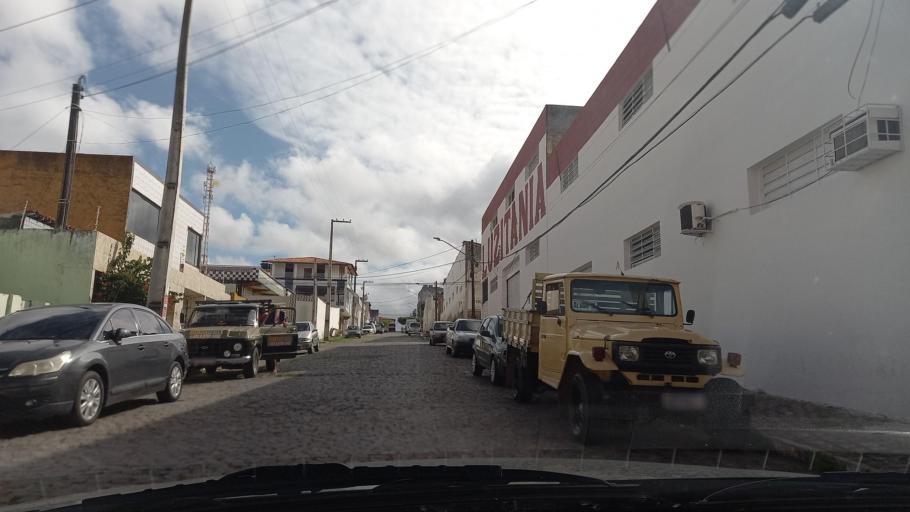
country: BR
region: Pernambuco
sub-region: Caruaru
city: Caruaru
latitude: -8.2878
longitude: -35.9821
